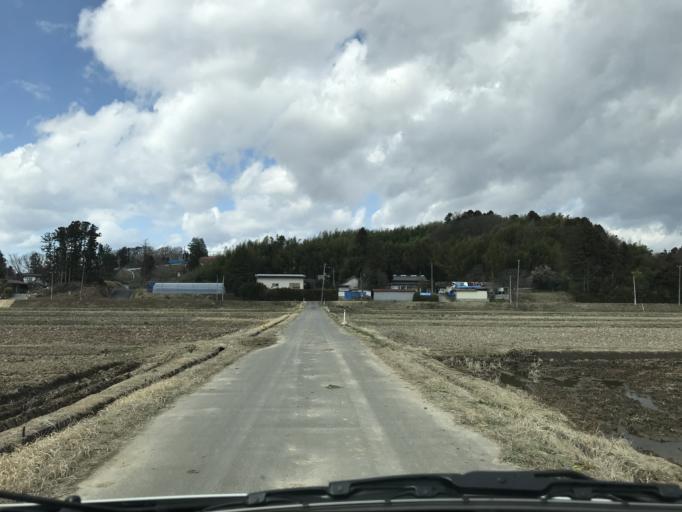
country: JP
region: Miyagi
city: Wakuya
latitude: 38.6902
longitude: 141.1476
